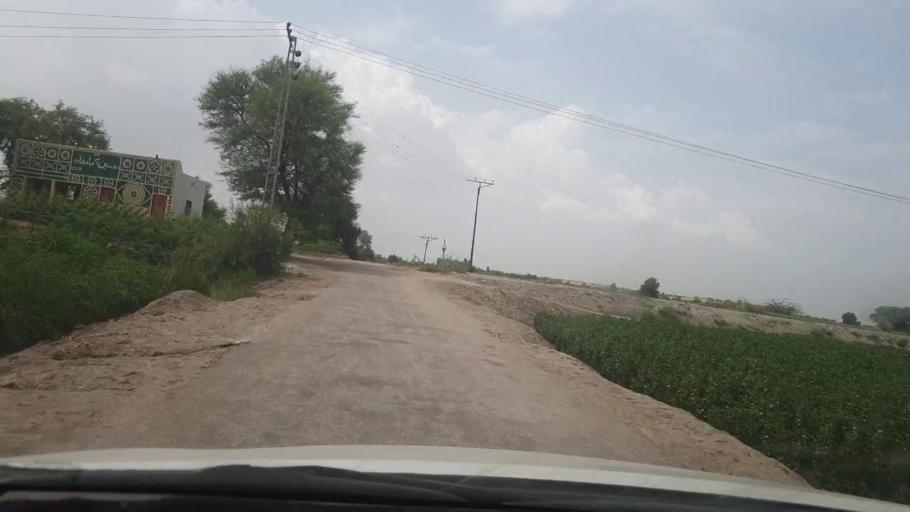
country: PK
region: Sindh
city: Kot Diji
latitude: 27.3111
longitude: 69.0115
